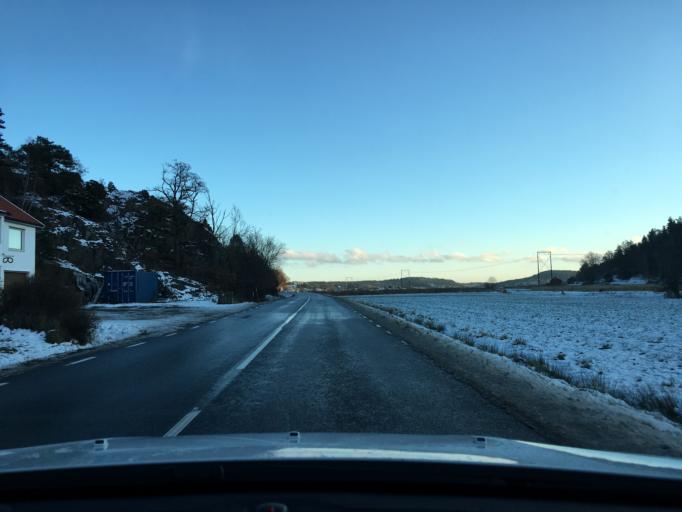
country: SE
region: Vaestra Goetaland
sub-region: Tjorns Kommun
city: Myggenas
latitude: 58.1232
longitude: 11.7294
